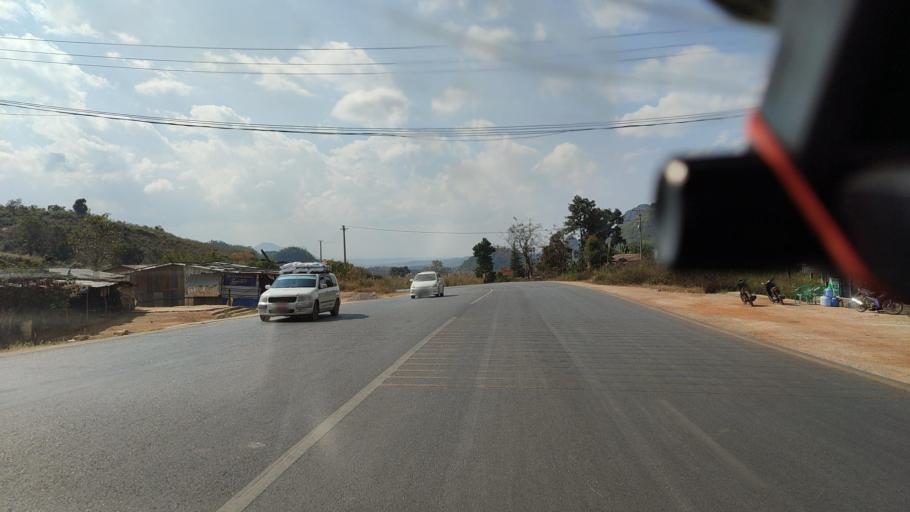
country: MM
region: Shan
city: Lashio
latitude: 23.0707
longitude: 97.7793
